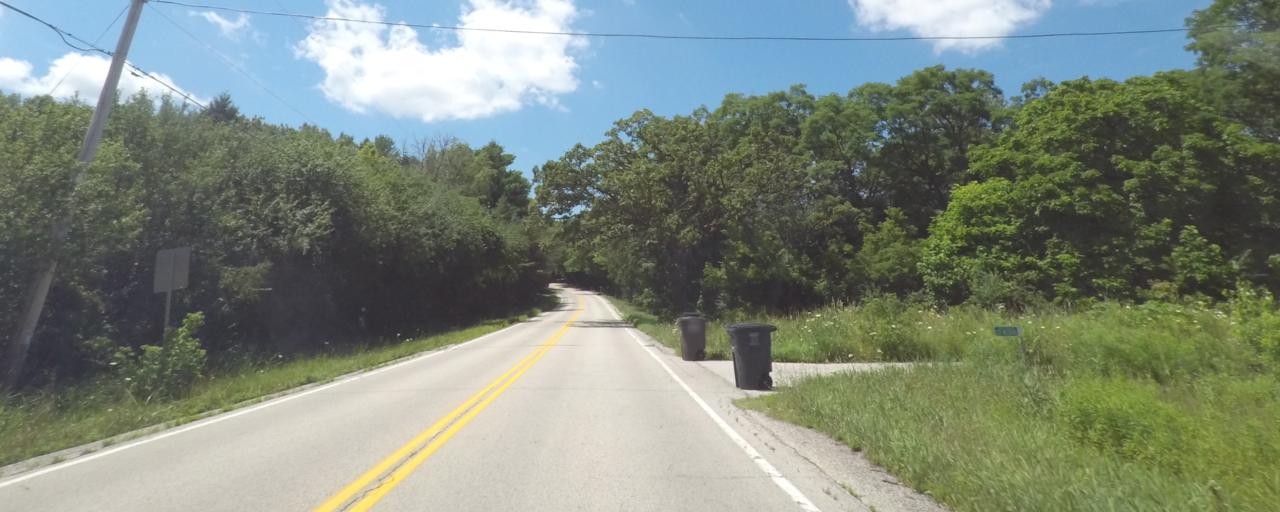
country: US
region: Wisconsin
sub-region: Waukesha County
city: Wales
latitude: 42.9874
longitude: -88.4149
